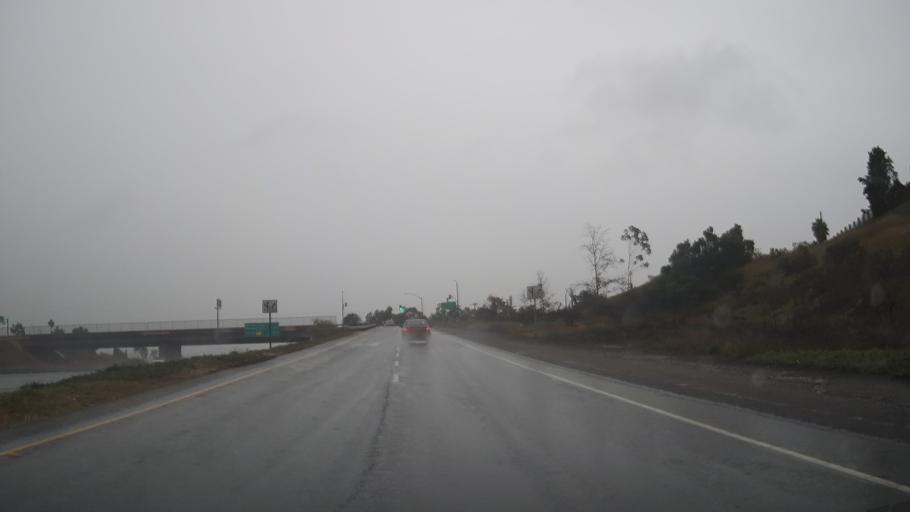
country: US
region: California
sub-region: San Diego County
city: Bonita
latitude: 32.6635
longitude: -117.0593
